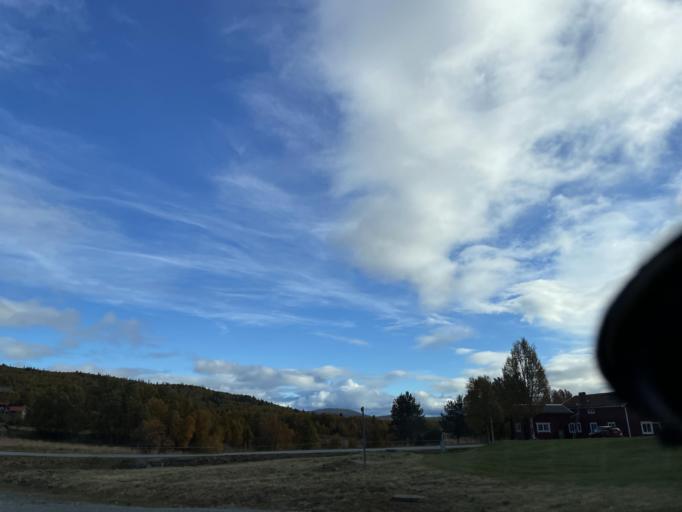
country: NO
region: Sor-Trondelag
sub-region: Tydal
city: Aas
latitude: 62.6391
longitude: 12.4370
